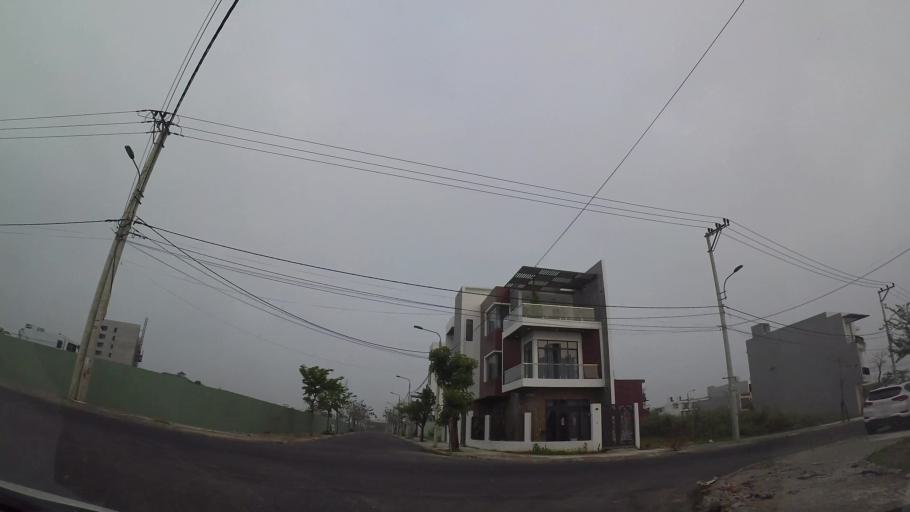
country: VN
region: Da Nang
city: Ngu Hanh Son
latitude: 16.0194
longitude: 108.2336
